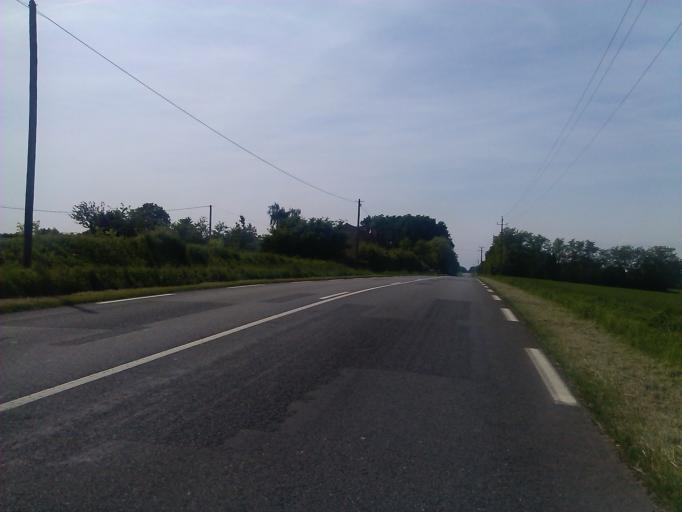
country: FR
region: Centre
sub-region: Departement de l'Indre
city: La Chatre
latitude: 46.5541
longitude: 2.0860
